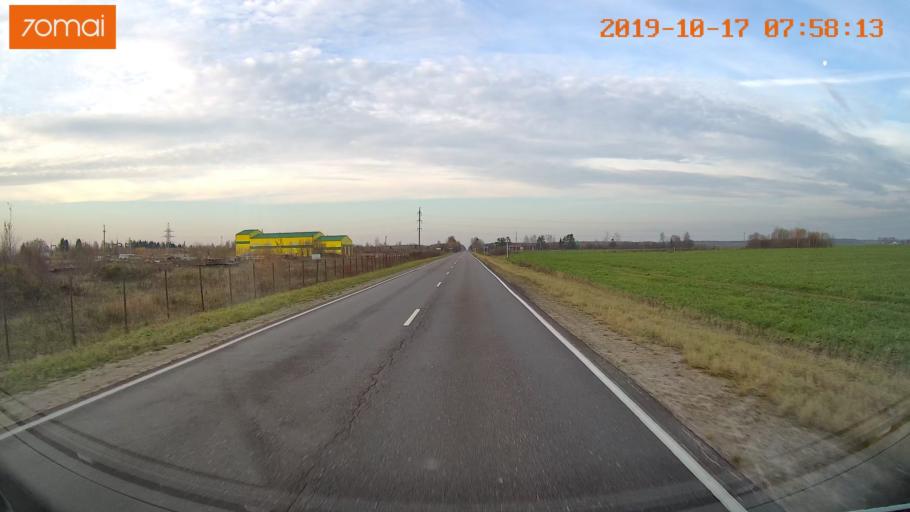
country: RU
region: Vladimir
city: Bavleny
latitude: 56.4047
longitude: 39.5619
